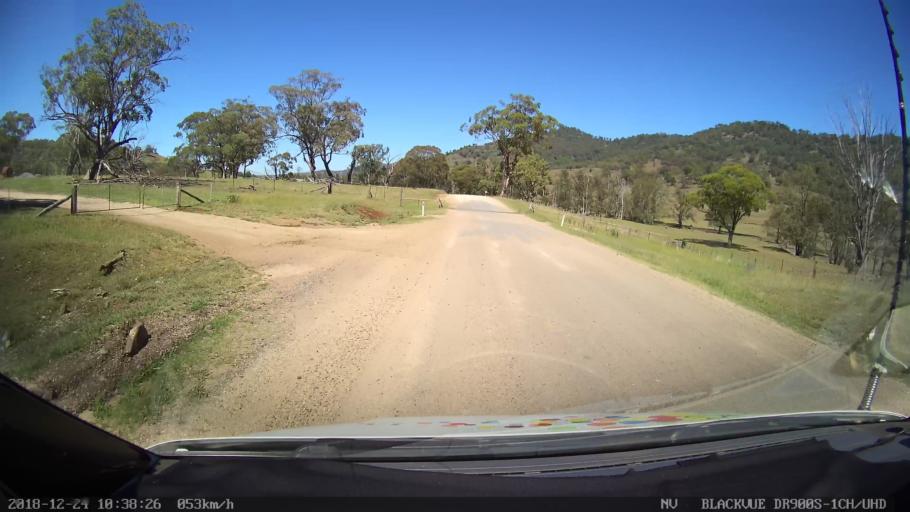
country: AU
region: New South Wales
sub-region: Upper Hunter Shire
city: Merriwa
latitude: -31.8488
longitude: 150.4822
